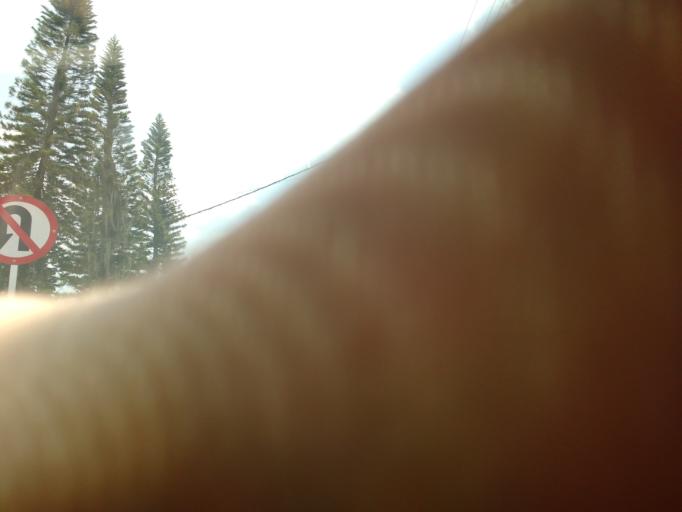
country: CO
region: Cundinamarca
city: Fusagasuga
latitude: 4.3327
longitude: -74.3721
